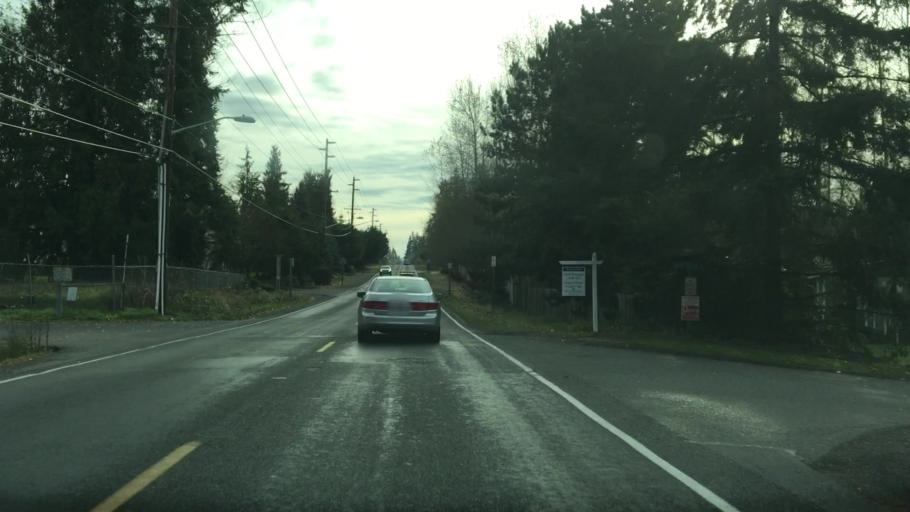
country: US
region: Washington
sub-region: Pierce County
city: South Hill
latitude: 47.1371
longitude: -122.3150
